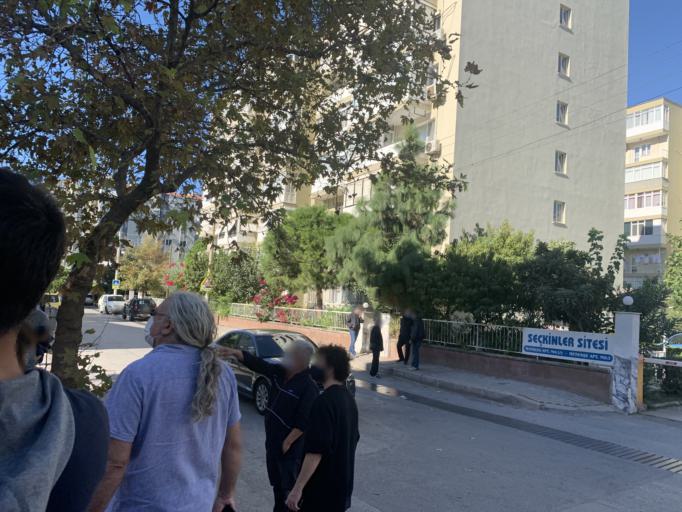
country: TR
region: Izmir
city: Bornova
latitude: 38.4635
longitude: 27.1898
